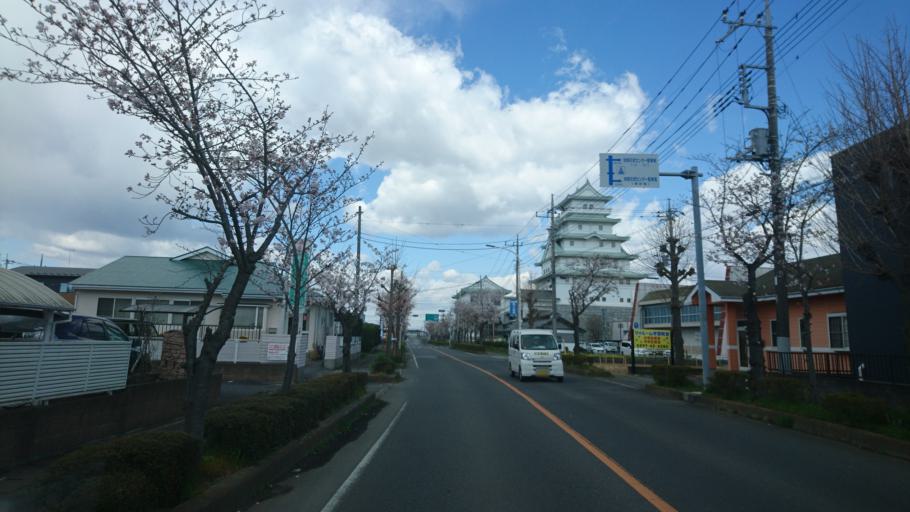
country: JP
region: Ibaraki
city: Ishige
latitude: 36.1118
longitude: 139.9804
